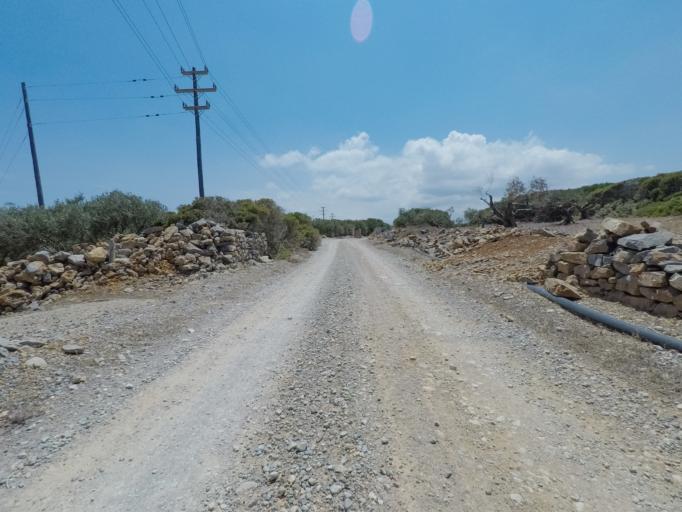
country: GR
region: Crete
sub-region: Nomos Lasithiou
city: Elounda
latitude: 35.3223
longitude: 25.7534
